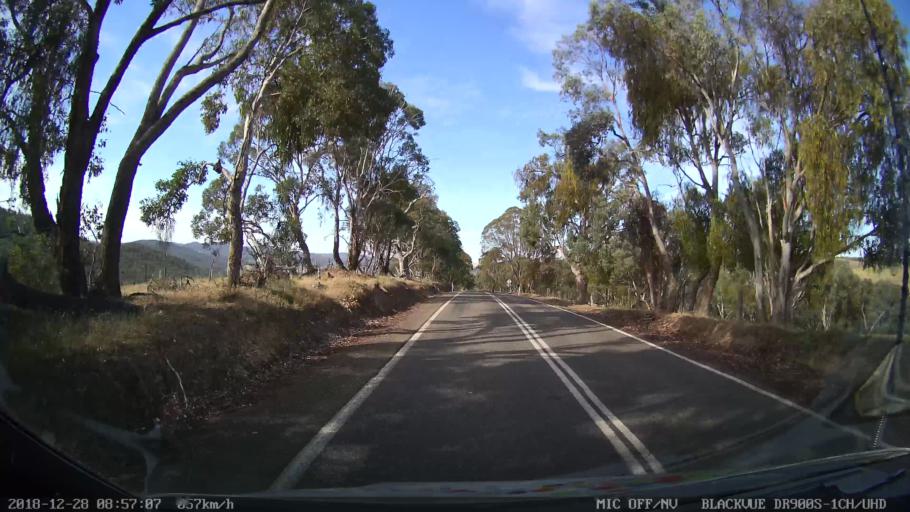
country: AU
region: New South Wales
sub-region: Upper Lachlan Shire
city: Crookwell
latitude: -34.1165
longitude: 149.3374
